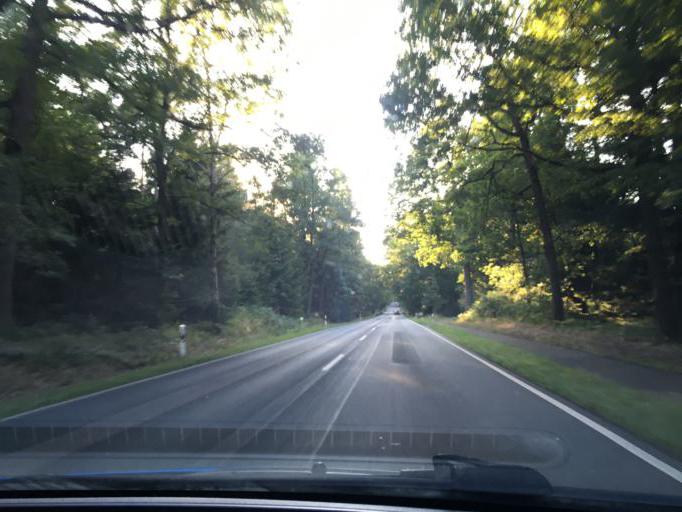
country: DE
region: Lower Saxony
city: Unterluss
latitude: 52.8077
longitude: 10.3633
